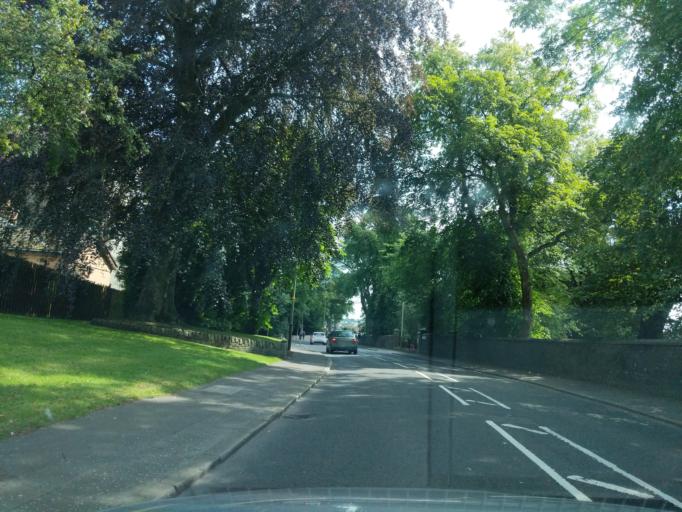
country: GB
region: Scotland
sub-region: Dundee City
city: Dundee
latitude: 56.4787
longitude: -3.0189
